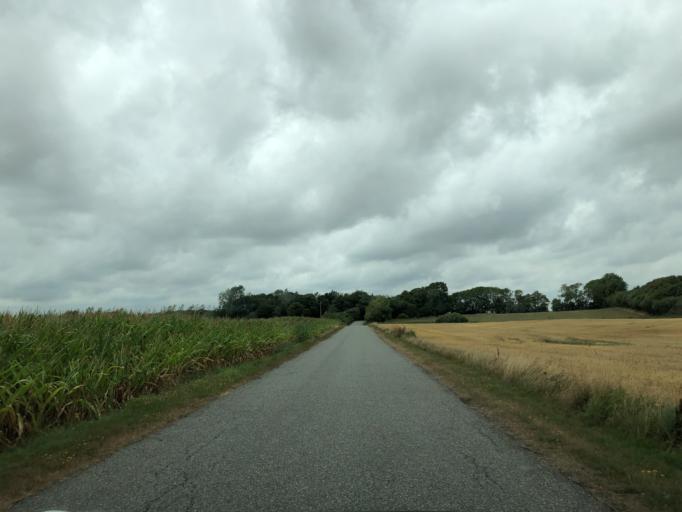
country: DK
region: Central Jutland
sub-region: Ringkobing-Skjern Kommune
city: Videbaek
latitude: 56.0990
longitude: 8.4893
